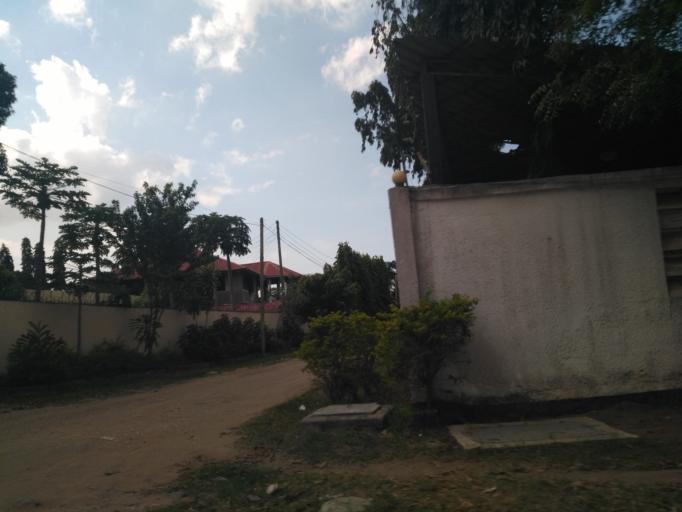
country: TZ
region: Dar es Salaam
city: Magomeni
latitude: -6.7761
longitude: 39.2585
